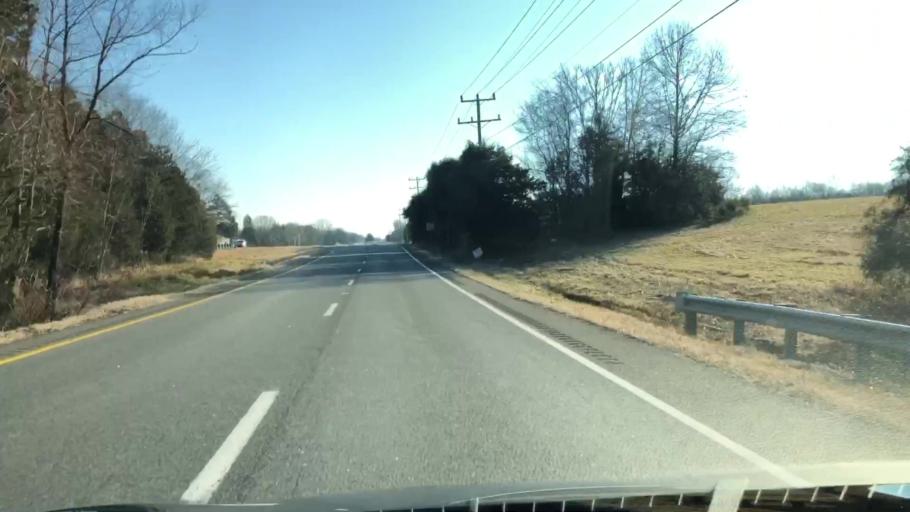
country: US
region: Virginia
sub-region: Fauquier County
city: Bealeton
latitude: 38.5770
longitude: -77.8021
